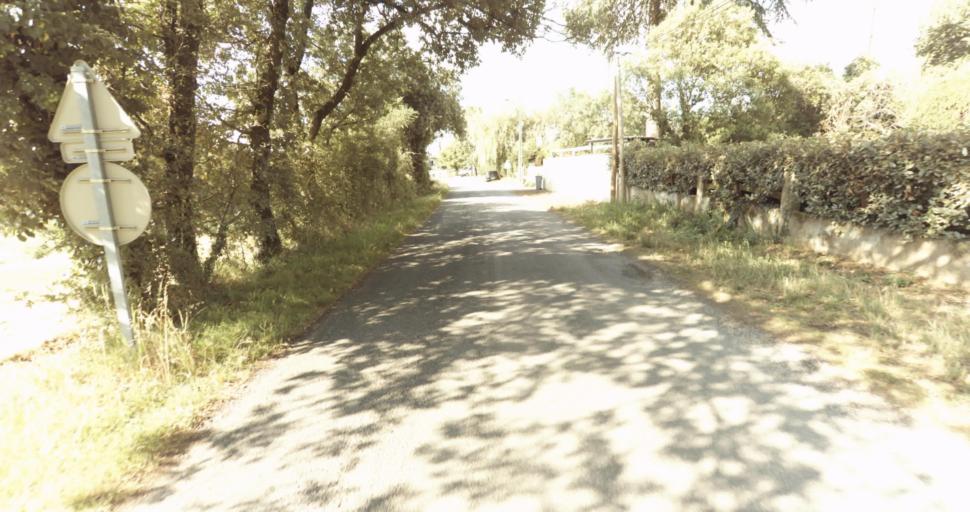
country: FR
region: Midi-Pyrenees
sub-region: Departement de la Haute-Garonne
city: Fontenilles
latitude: 43.5621
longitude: 1.2130
